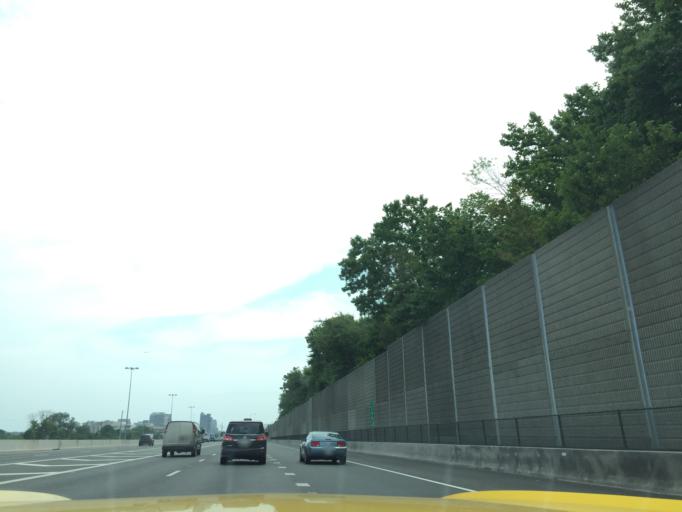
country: US
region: Virginia
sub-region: Fairfax County
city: Rose Hill
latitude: 38.8018
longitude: -77.0930
